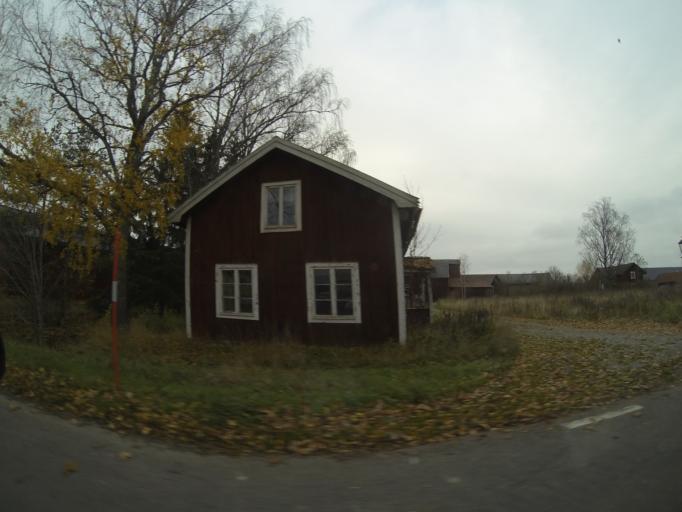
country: SE
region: Vaestmanland
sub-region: Vasteras
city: Skultuna
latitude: 59.6835
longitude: 16.4402
